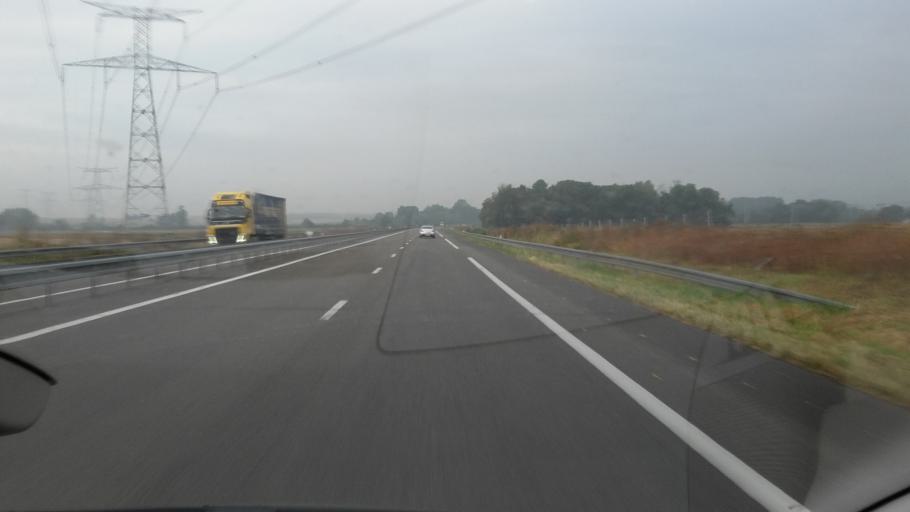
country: FR
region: Champagne-Ardenne
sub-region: Departement des Ardennes
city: Rethel
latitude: 49.5648
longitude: 4.4683
